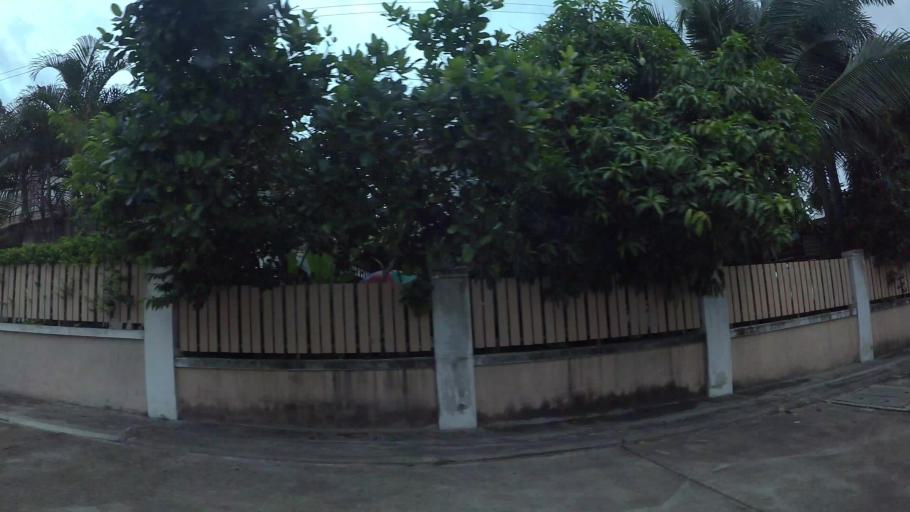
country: TH
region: Chon Buri
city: Si Racha
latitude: 13.2076
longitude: 100.9478
